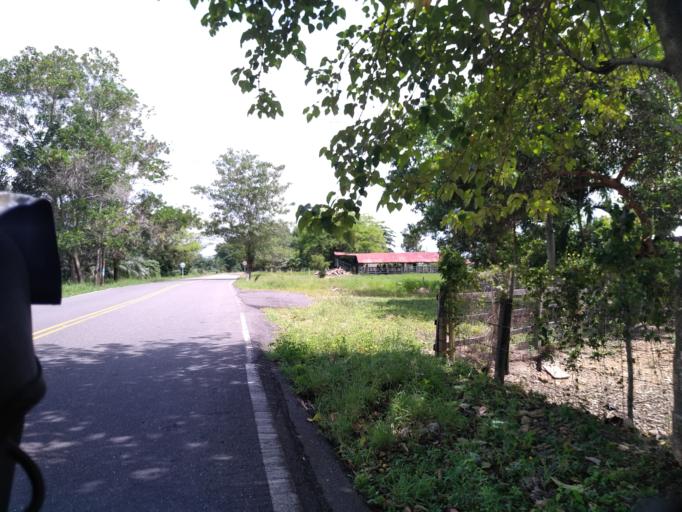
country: CO
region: Santander
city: Puerto Parra
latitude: 6.4941
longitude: -74.0490
